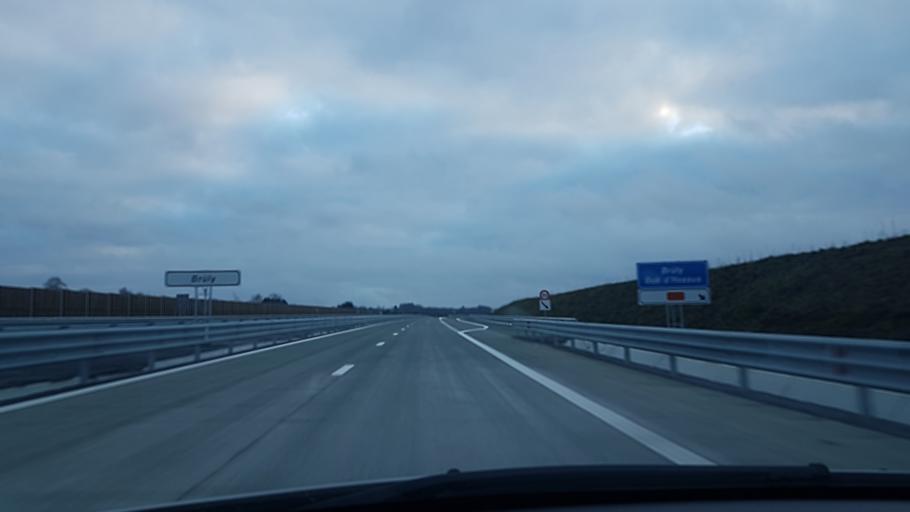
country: FR
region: Champagne-Ardenne
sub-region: Departement des Ardennes
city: Rocroi
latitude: 49.9668
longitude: 4.5362
